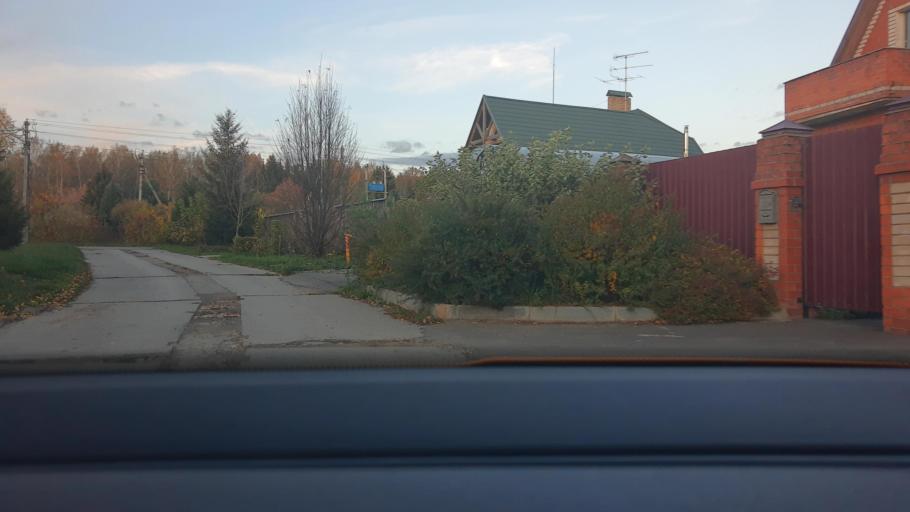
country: RU
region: Moskovskaya
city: Sheremet'yevskiy
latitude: 56.0026
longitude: 37.5273
